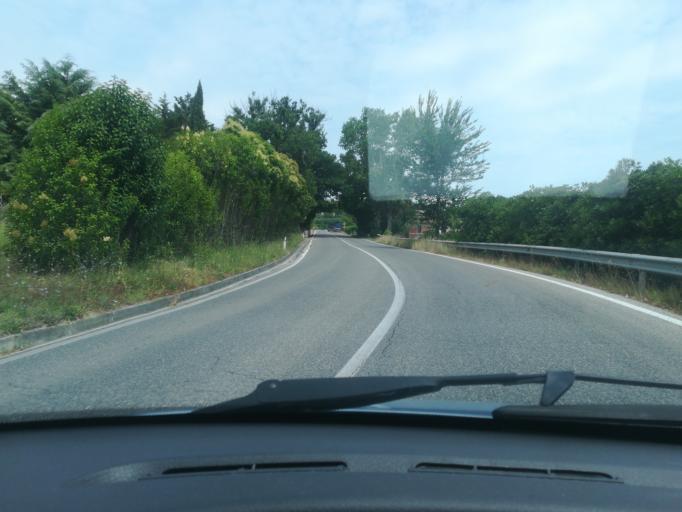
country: IT
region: The Marches
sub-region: Provincia di Macerata
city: Recanati
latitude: 43.3936
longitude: 13.5376
